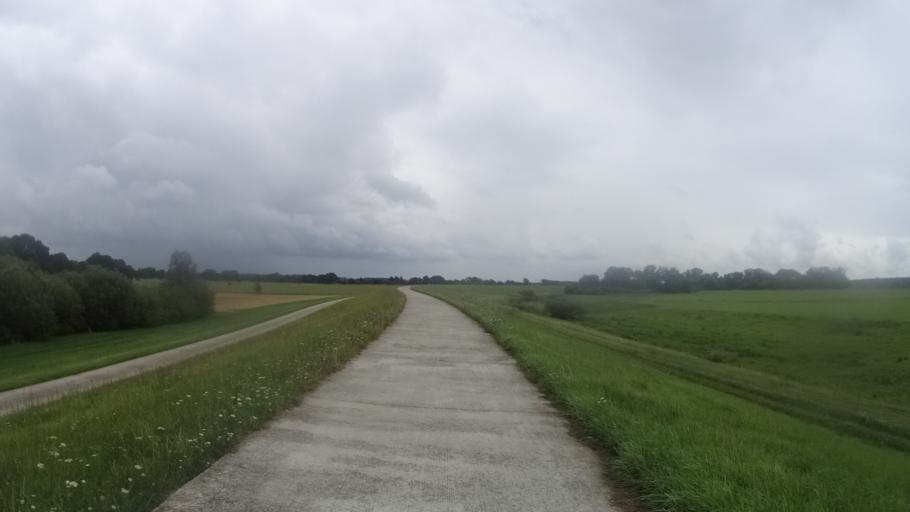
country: DE
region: Lower Saxony
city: Bleckede
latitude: 53.2977
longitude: 10.7858
